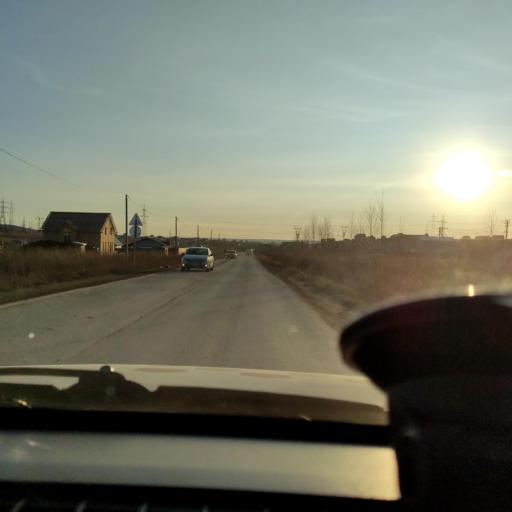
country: RU
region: Perm
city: Ferma
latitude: 57.9544
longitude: 56.3694
